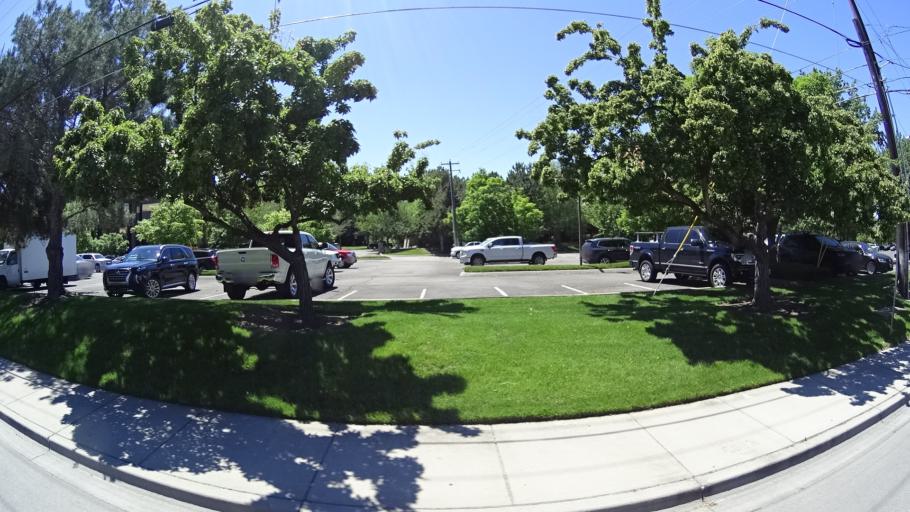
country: US
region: Idaho
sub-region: Ada County
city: Boise
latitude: 43.6128
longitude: -116.2128
